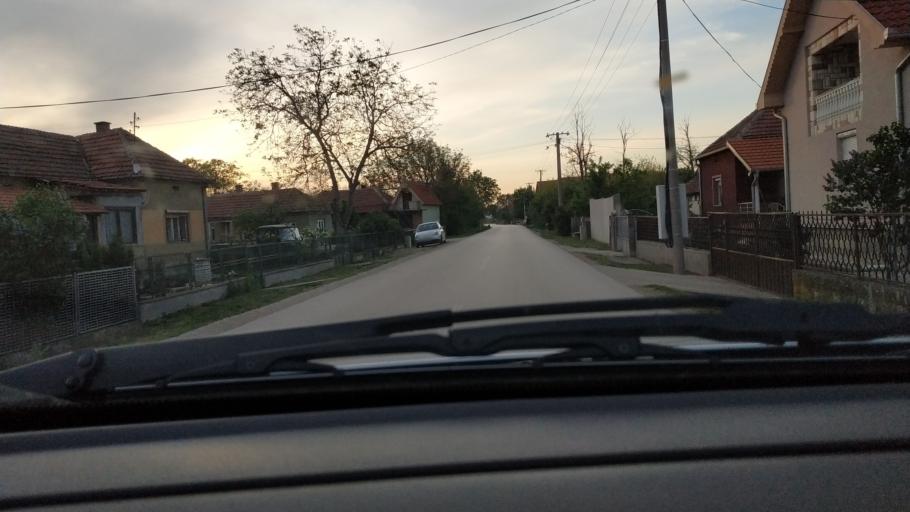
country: RS
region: Central Serbia
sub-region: Nisavski Okrug
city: Aleksinac
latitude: 43.5441
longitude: 21.6264
